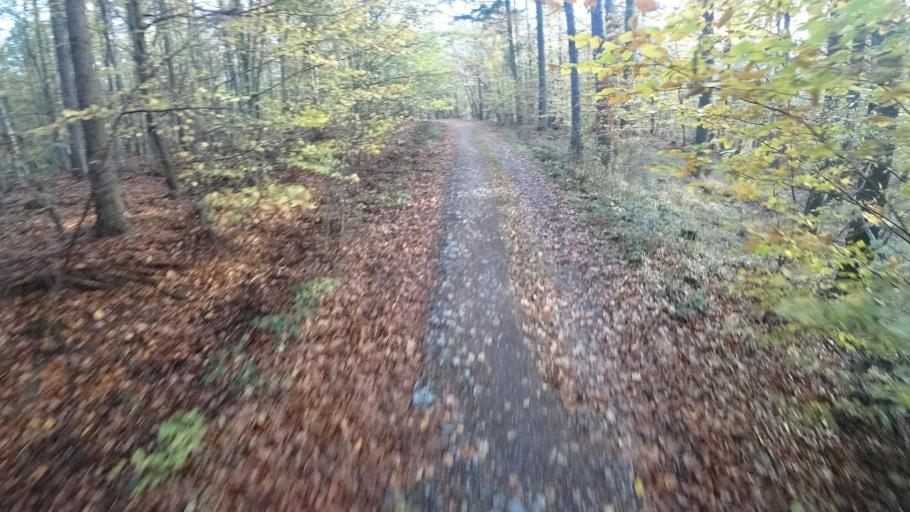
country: DE
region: Rheinland-Pfalz
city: Berg
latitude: 50.5487
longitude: 6.9648
